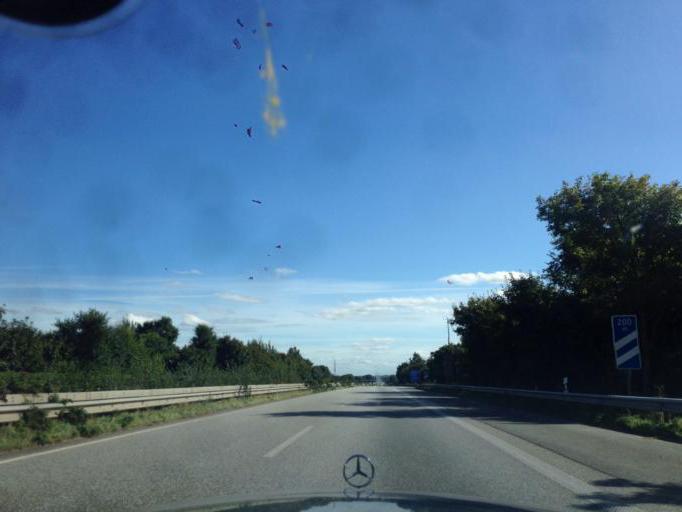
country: DE
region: Schleswig-Holstein
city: Jarplund-Weding
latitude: 54.7397
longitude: 9.3838
